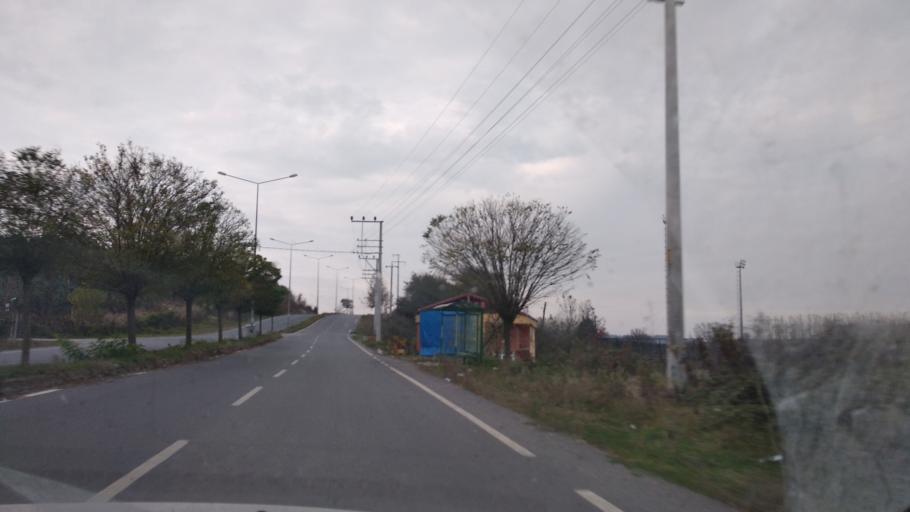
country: TR
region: Sakarya
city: Ortakoy
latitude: 41.0430
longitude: 30.6397
